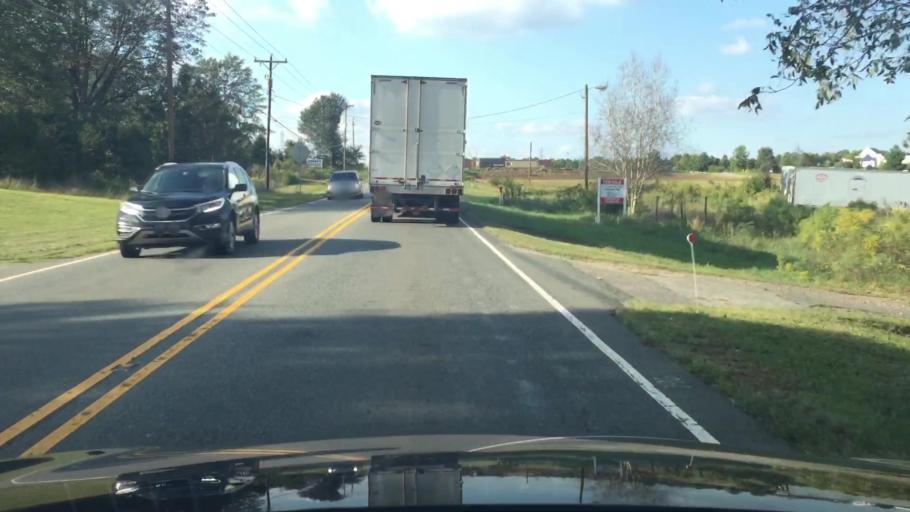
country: US
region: North Carolina
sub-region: Iredell County
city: Troutman
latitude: 35.6668
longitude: -80.8521
